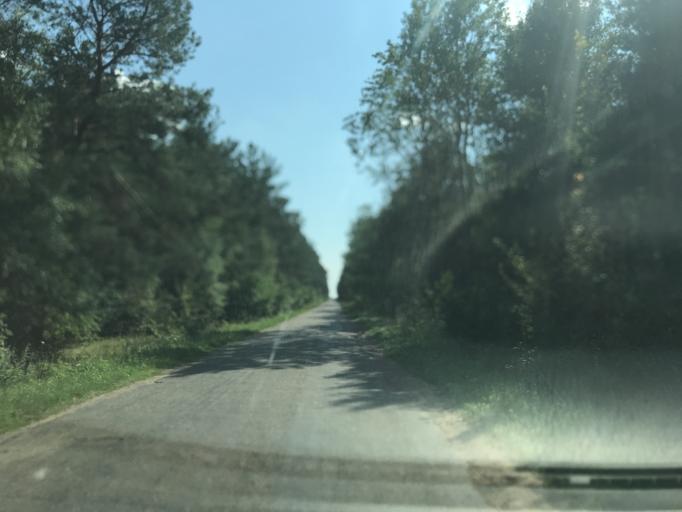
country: PL
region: Masovian Voivodeship
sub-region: Powiat zurominski
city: Zuromin
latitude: 53.1490
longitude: 19.9344
